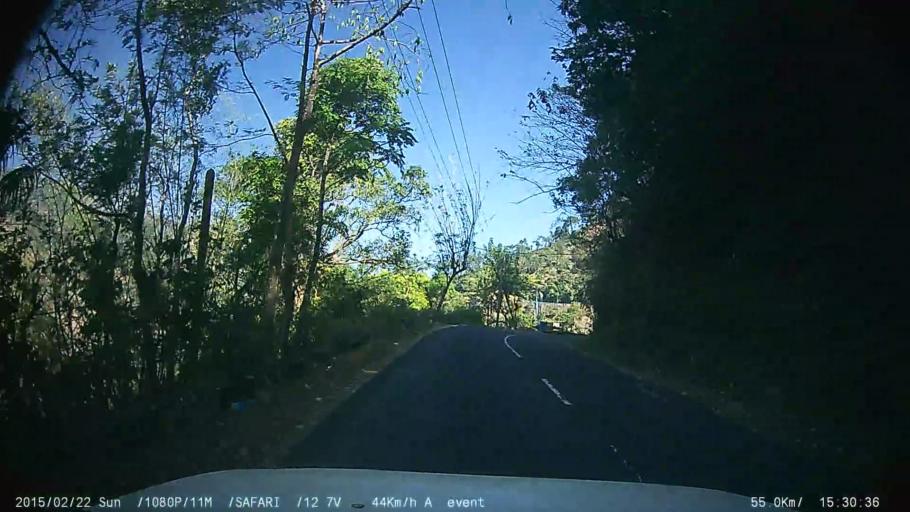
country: IN
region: Kerala
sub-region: Kottayam
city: Erattupetta
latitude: 9.5603
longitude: 76.9547
